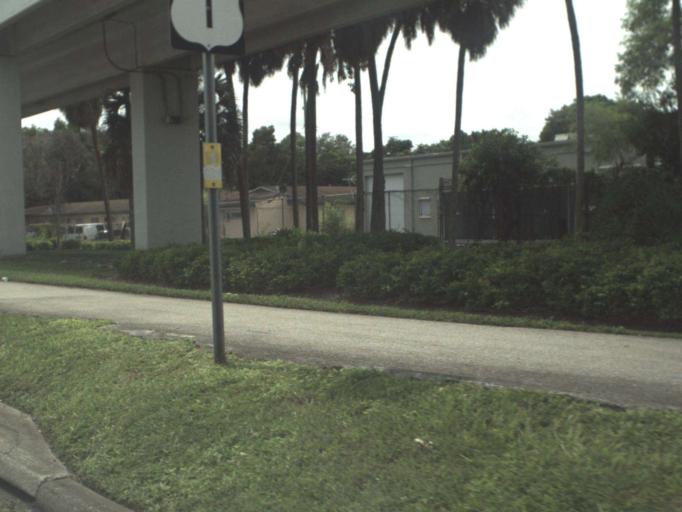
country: US
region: Florida
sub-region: Miami-Dade County
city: South Miami
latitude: 25.6992
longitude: -80.2961
